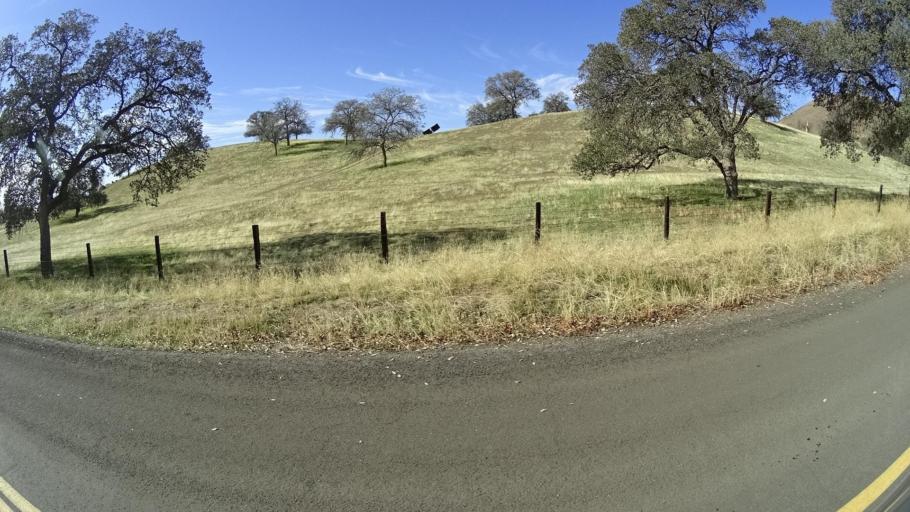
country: US
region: California
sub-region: Tulare County
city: Richgrove
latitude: 35.6810
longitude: -118.8453
